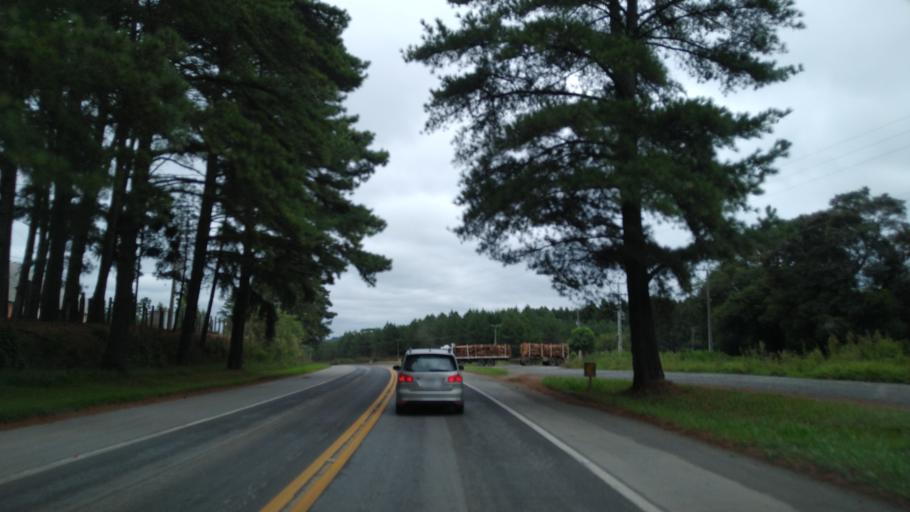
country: BR
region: Santa Catarina
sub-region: Tres Barras
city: Tres Barras
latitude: -26.1613
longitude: -50.1307
